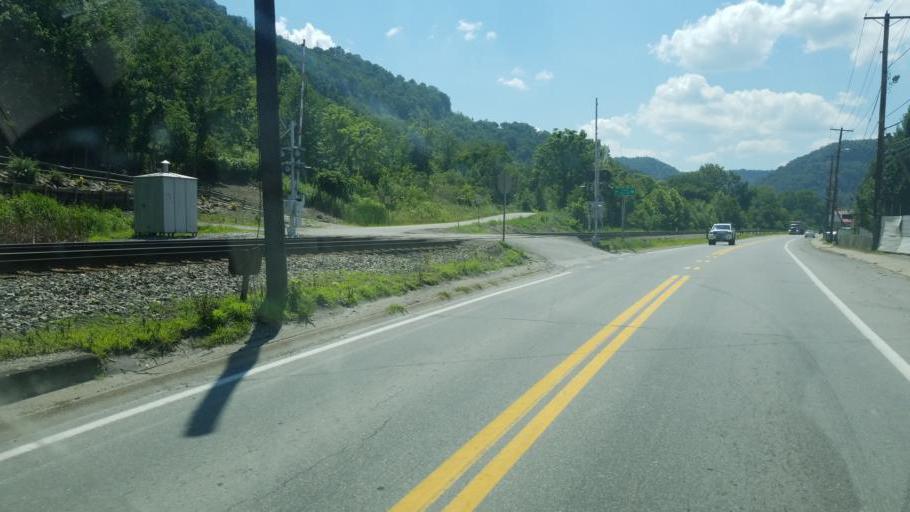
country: US
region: West Virginia
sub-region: Kanawha County
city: Chesapeake
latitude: 38.1953
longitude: -81.4842
